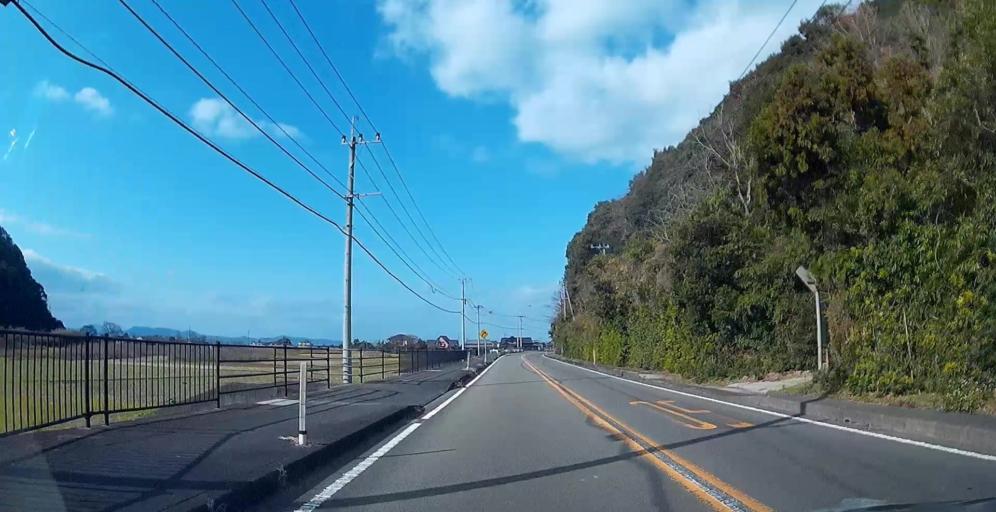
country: JP
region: Kumamoto
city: Yatsushiro
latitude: 32.4147
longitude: 130.5508
